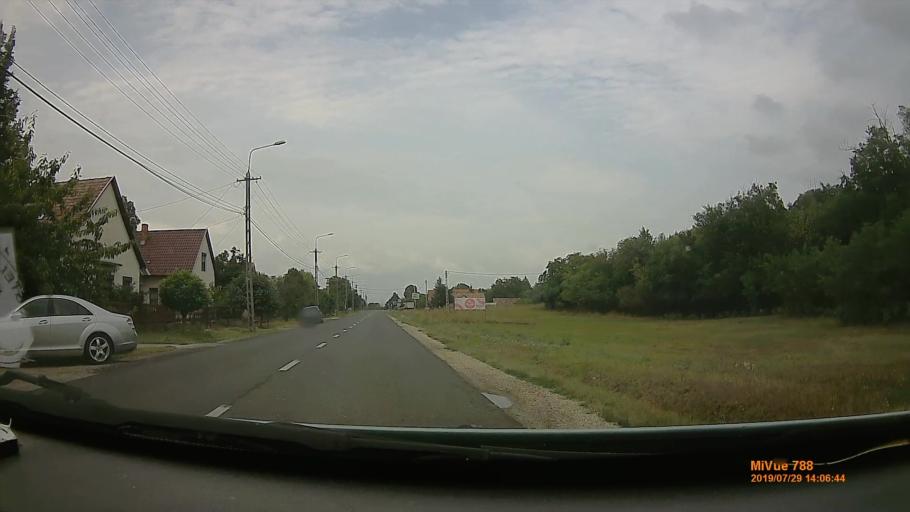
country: HU
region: Somogy
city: Balatonfoldvar
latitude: 46.8195
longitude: 17.9065
